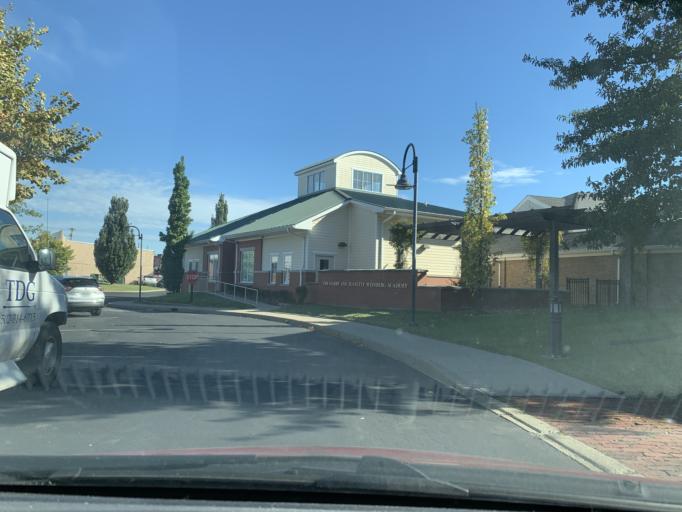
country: US
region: Indiana
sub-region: Clark County
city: Jeffersonville
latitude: 38.2525
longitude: -85.7307
